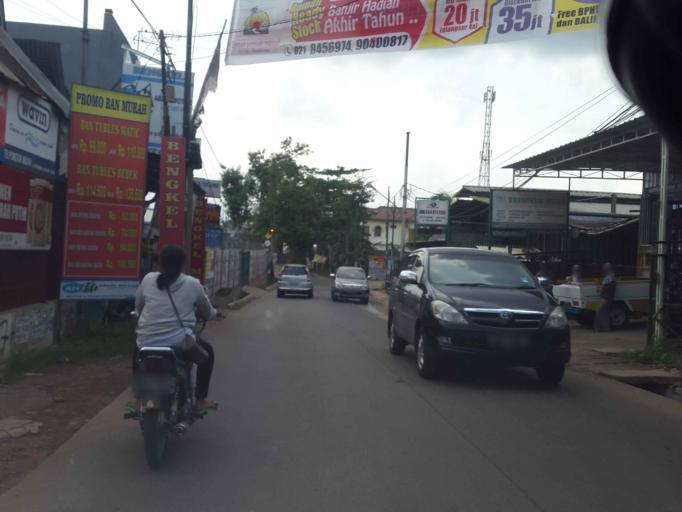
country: ID
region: West Java
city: Cileungsir
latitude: -6.3177
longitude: 106.9492
